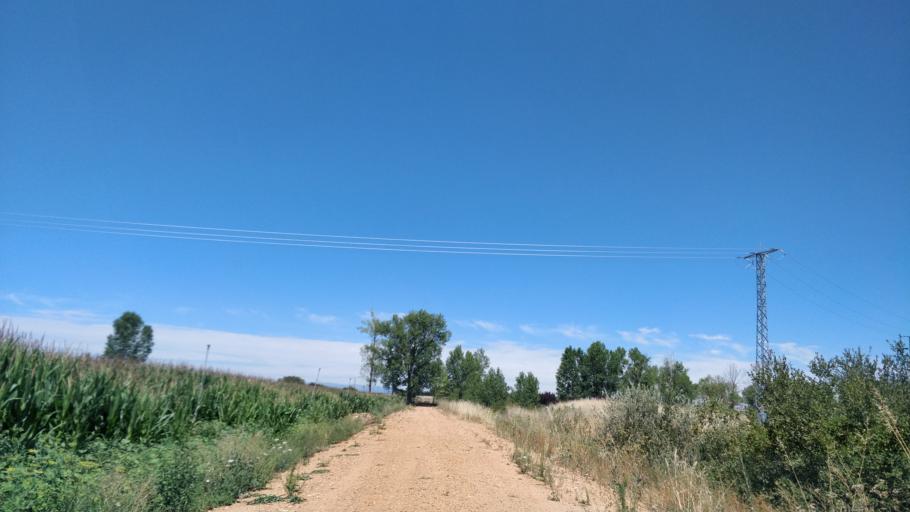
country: ES
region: Castille and Leon
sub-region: Provincia de Leon
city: Bustillo del Paramo
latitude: 42.4779
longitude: -5.8111
